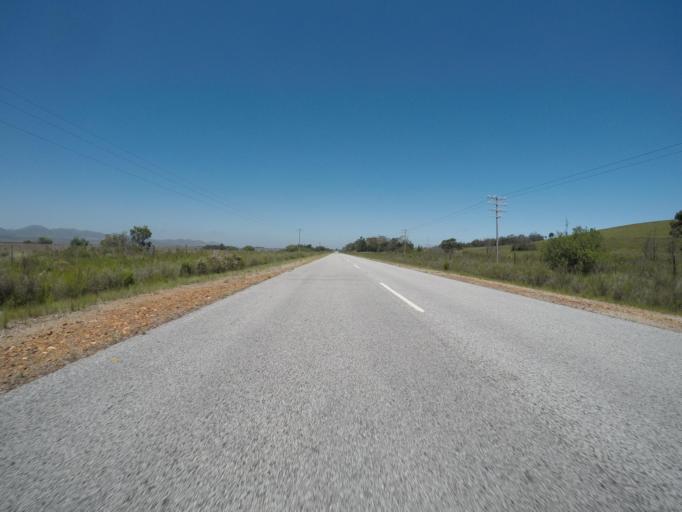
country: ZA
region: Eastern Cape
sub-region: Cacadu District Municipality
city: Kruisfontein
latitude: -33.9835
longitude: 24.5122
